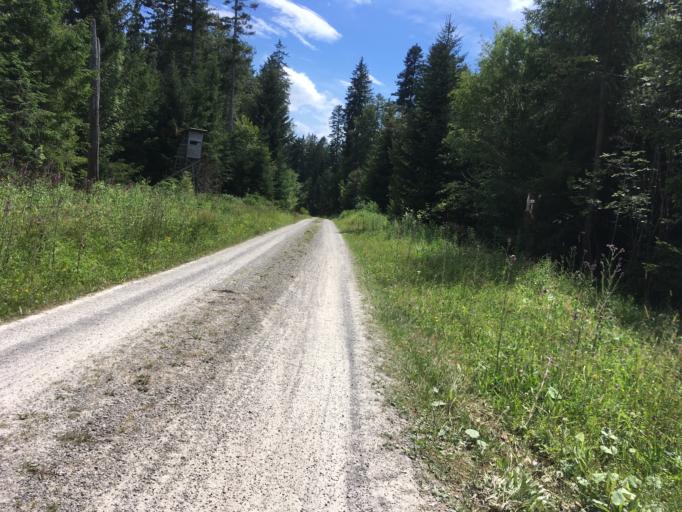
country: DE
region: Baden-Wuerttemberg
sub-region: Karlsruhe Region
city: Freudenstadt
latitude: 48.5127
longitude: 8.4259
